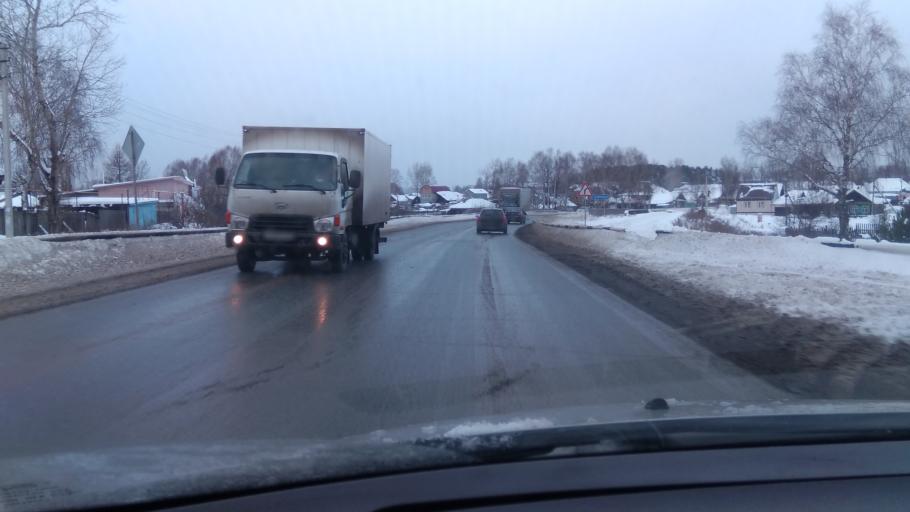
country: RU
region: Sverdlovsk
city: Nikolo-Pavlovskoye
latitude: 57.7846
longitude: 60.0572
